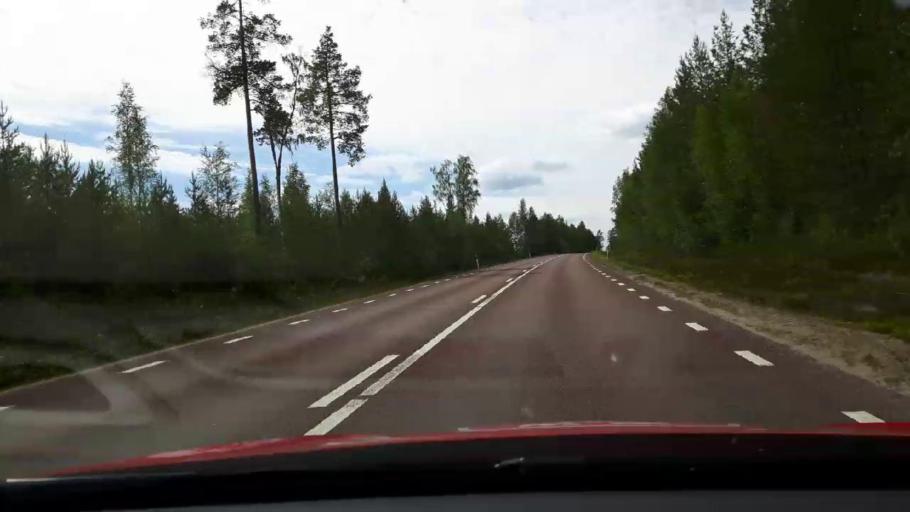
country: SE
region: Jaemtland
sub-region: Harjedalens Kommun
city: Sveg
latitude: 62.0499
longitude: 14.8928
